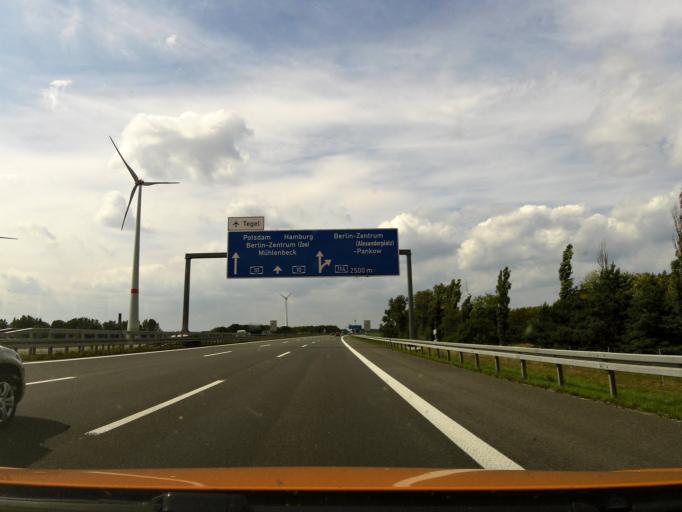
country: DE
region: Berlin
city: Karow
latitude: 52.6315
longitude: 13.4546
